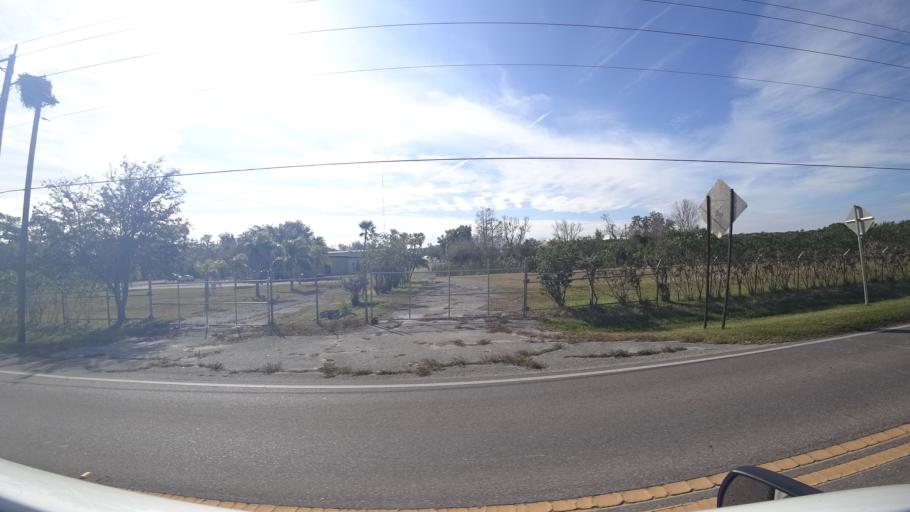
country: US
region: Florida
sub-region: Manatee County
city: Memphis
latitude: 27.6014
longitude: -82.5161
